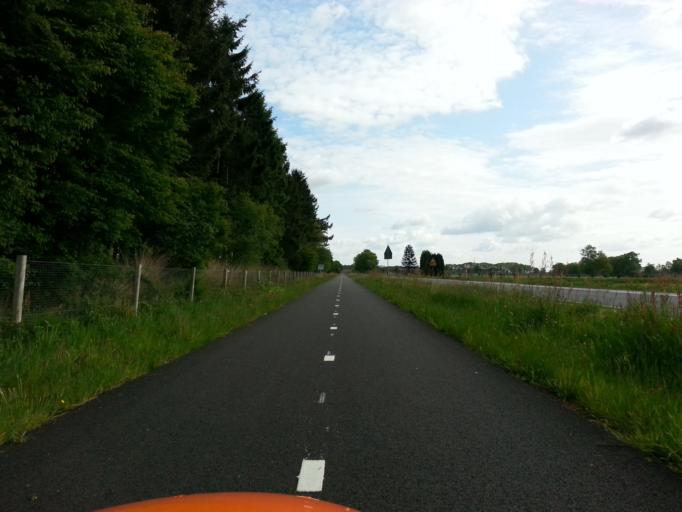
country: NL
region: Gelderland
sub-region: Gemeente Barneveld
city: Terschuur
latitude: 52.1049
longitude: 5.5232
